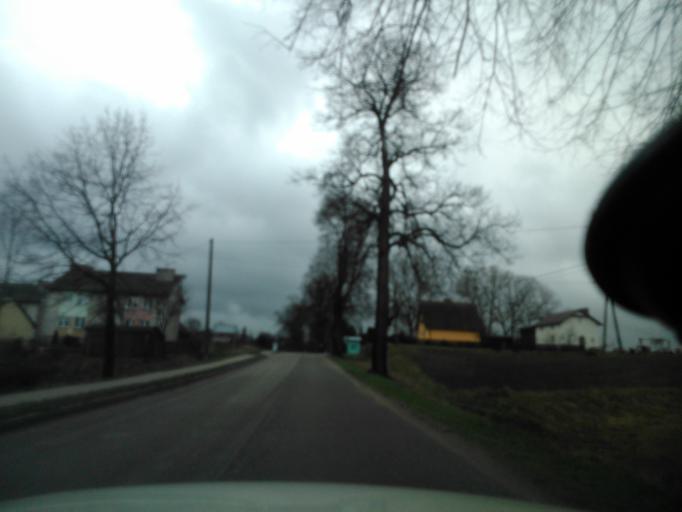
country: PL
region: Warmian-Masurian Voivodeship
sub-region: Powiat ostrodzki
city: Dabrowno
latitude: 53.4709
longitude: 20.0519
